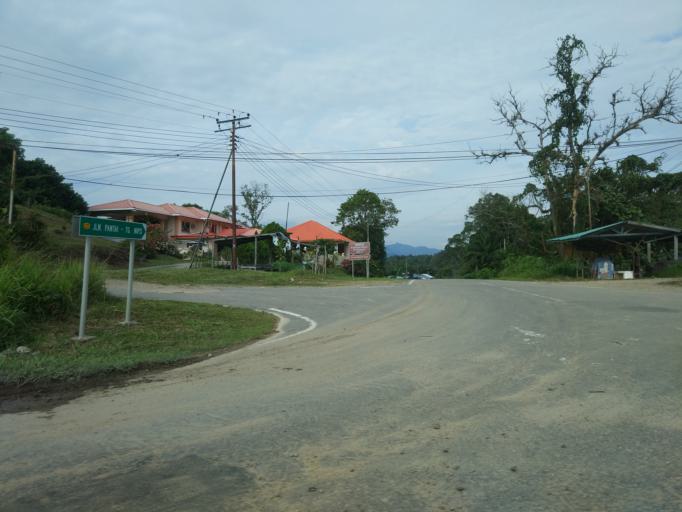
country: MY
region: Sabah
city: Beaufort
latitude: 4.9954
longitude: 115.5495
